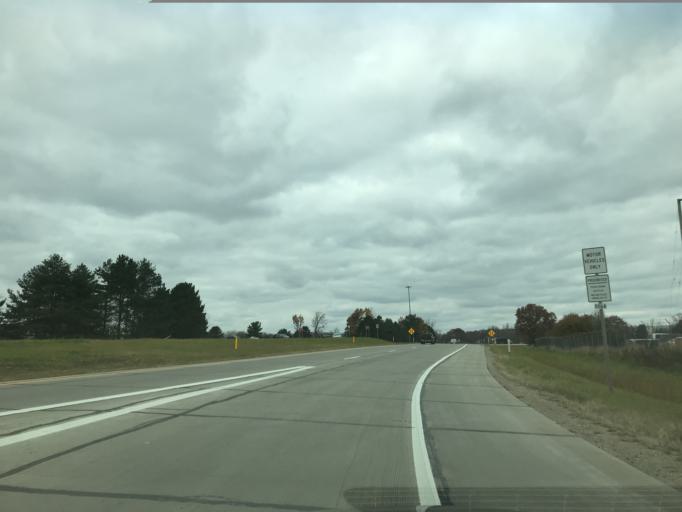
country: US
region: Michigan
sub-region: Eaton County
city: Waverly
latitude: 42.7416
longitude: -84.6655
